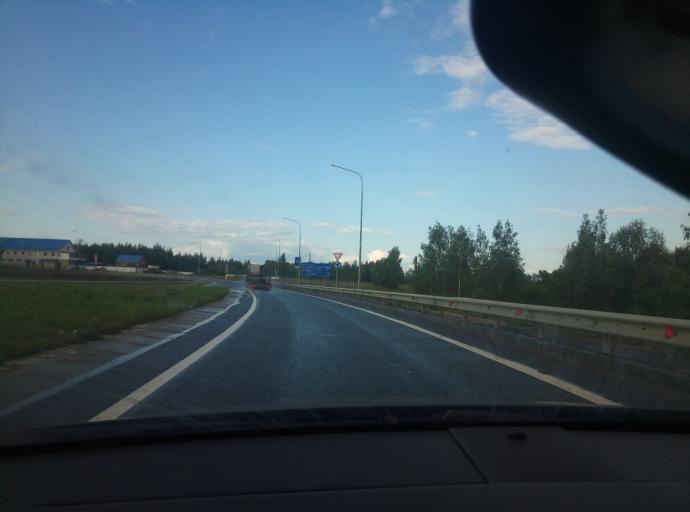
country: RU
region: Kaluga
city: Kurovskoye
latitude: 54.5272
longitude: 35.9882
